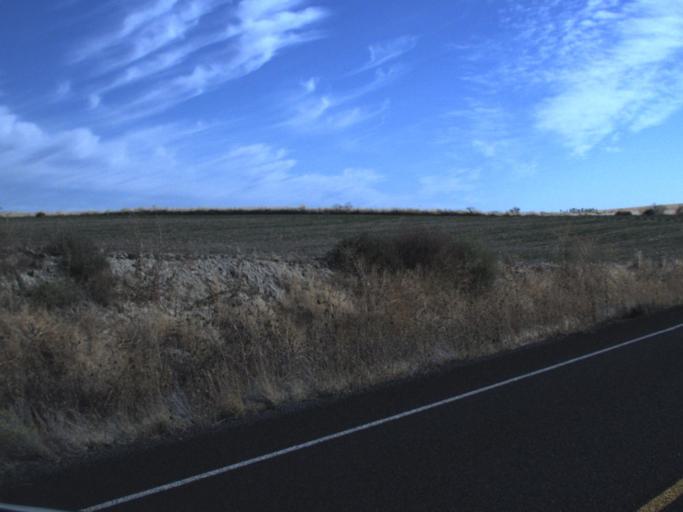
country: US
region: Washington
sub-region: Franklin County
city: Connell
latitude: 46.6201
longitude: -118.7041
